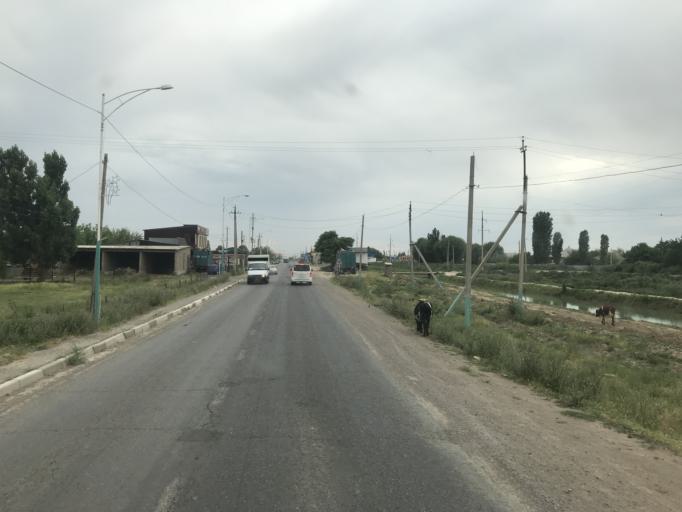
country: KZ
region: Ongtustik Qazaqstan
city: Asykata
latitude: 40.9037
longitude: 68.3630
